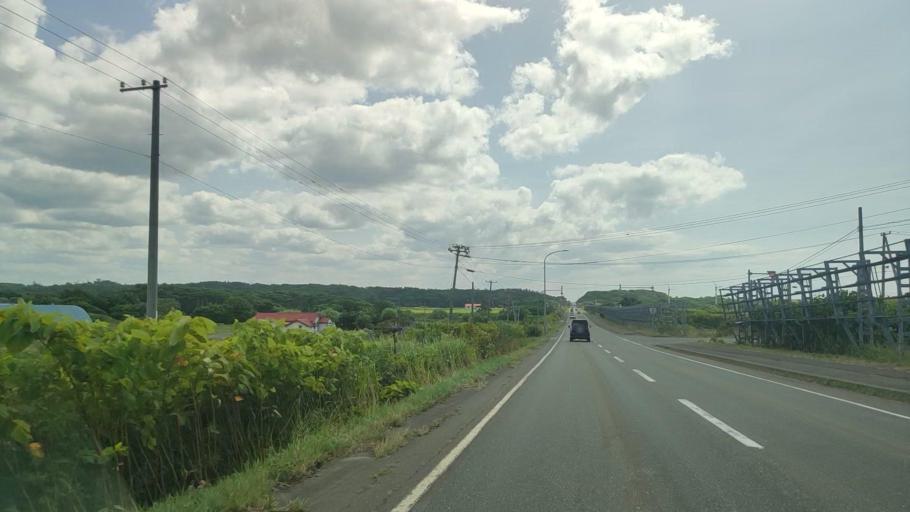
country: JP
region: Hokkaido
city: Makubetsu
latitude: 44.7758
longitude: 141.7917
